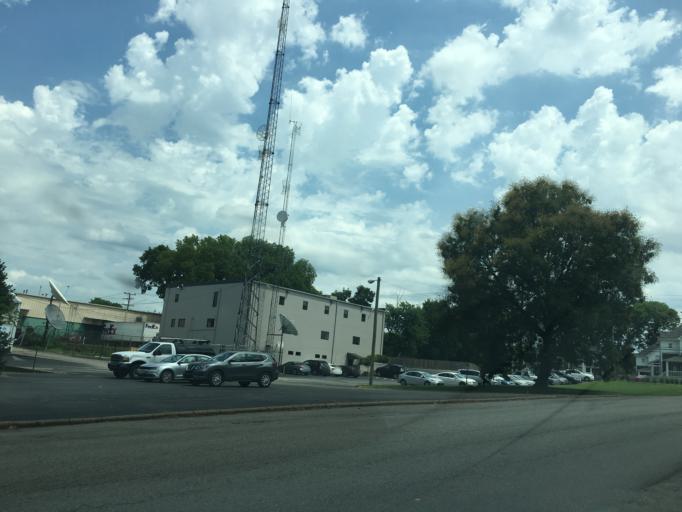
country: US
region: Tennessee
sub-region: Davidson County
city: Oak Hill
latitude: 36.1253
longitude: -86.7579
